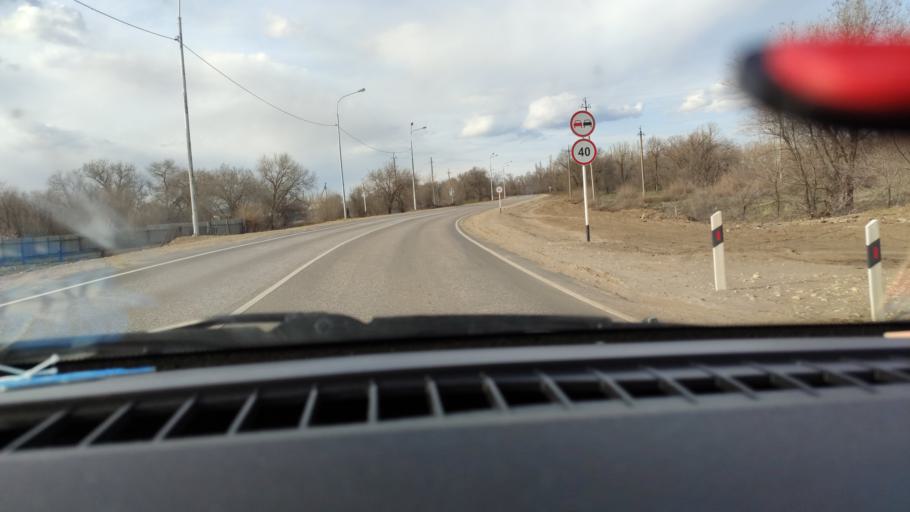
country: RU
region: Saratov
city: Krasnoarmeysk
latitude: 51.0895
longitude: 45.9573
